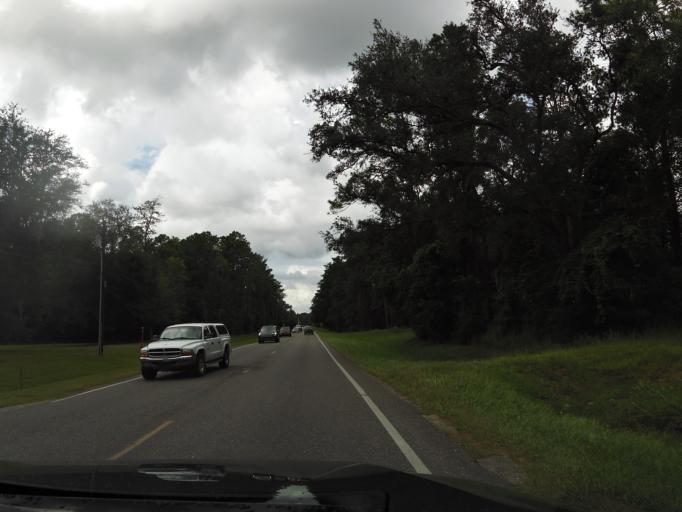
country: US
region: Florida
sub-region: Clay County
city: Middleburg
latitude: 30.0572
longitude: -81.8680
